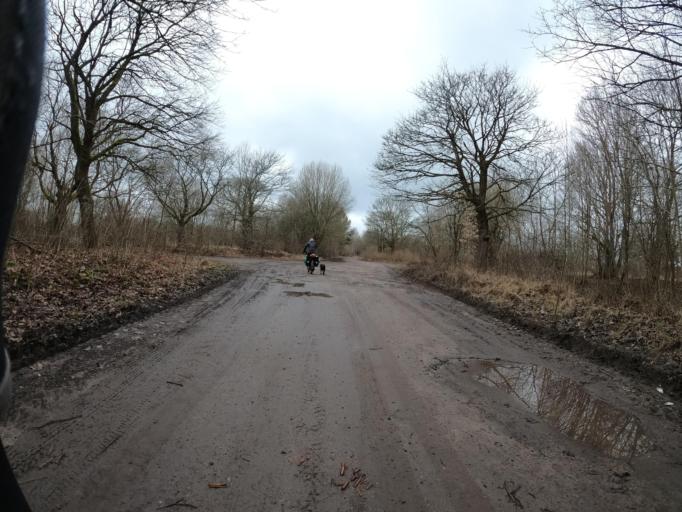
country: PL
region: Greater Poland Voivodeship
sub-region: Powiat zlotowski
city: Sypniewo
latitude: 53.4858
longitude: 16.5540
